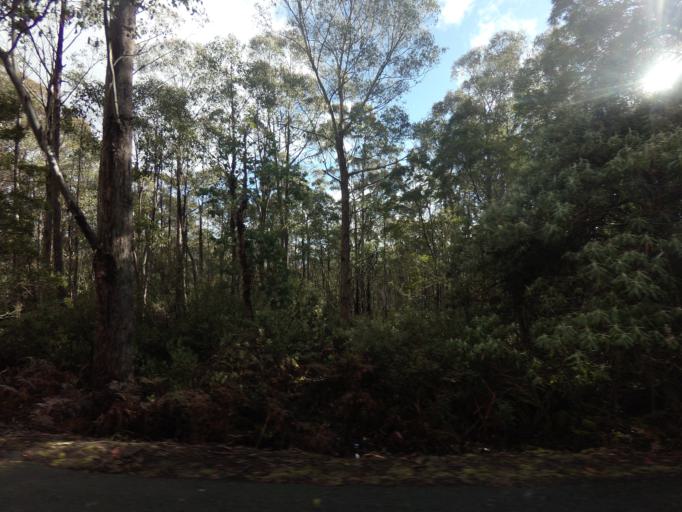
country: AU
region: Tasmania
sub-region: Glenorchy
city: Berriedale
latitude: -42.8420
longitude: 147.1489
